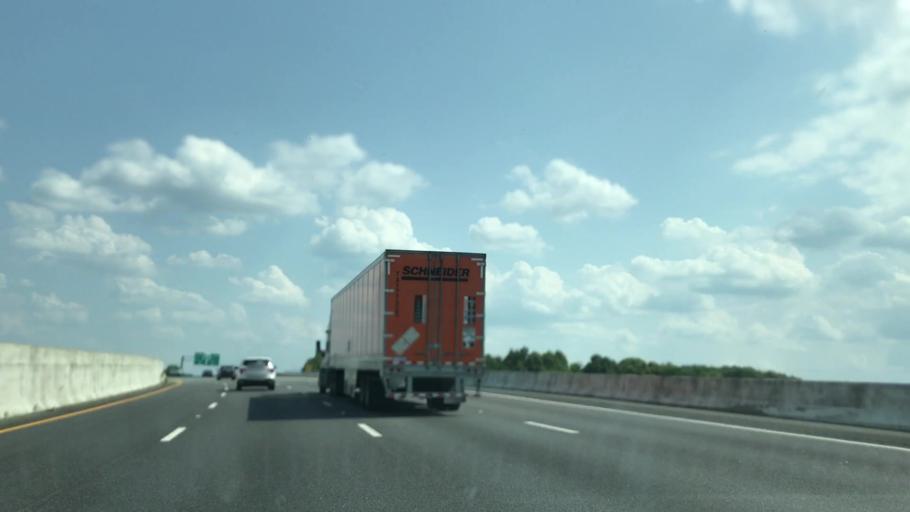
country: US
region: South Carolina
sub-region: York County
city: India Hook
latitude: 34.9778
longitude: -80.9884
